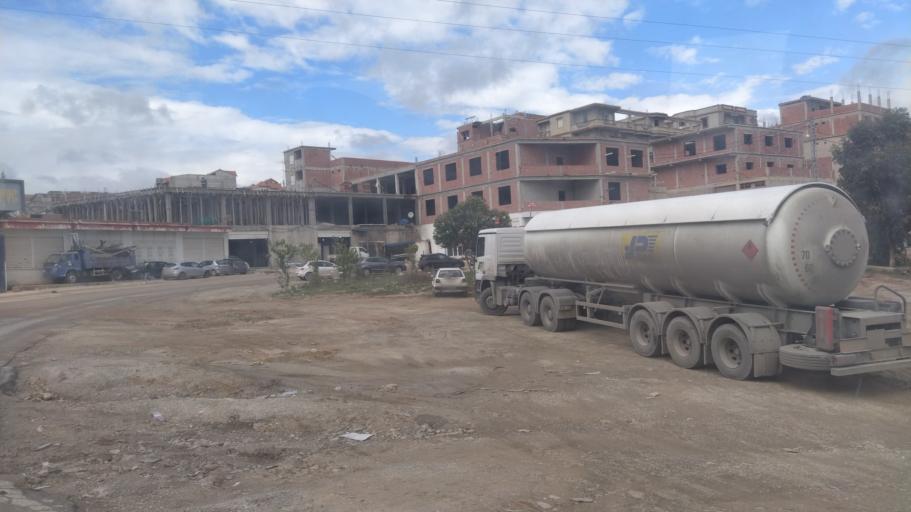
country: DZ
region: Constantine
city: El Khroub
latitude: 36.3050
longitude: 6.6845
